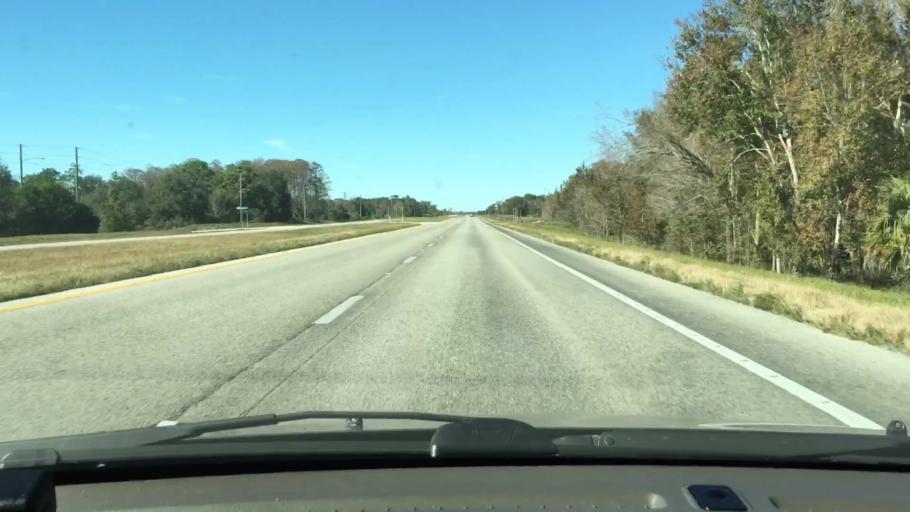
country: US
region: Florida
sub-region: Brevard County
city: June Park
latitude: 28.1236
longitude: -80.9626
